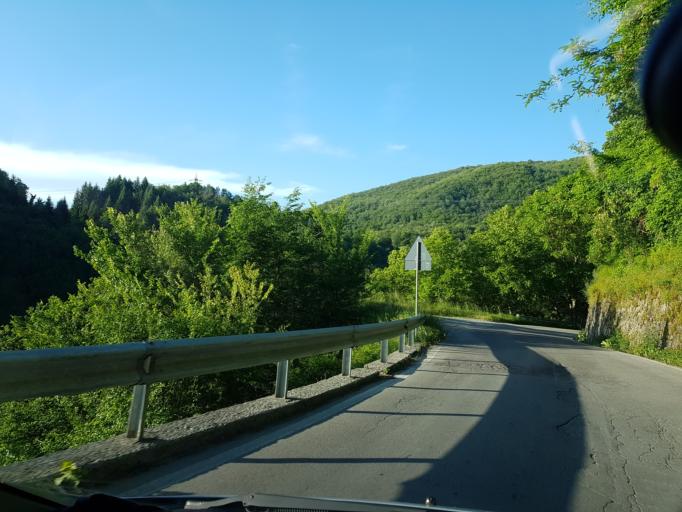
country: IT
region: Tuscany
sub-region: Provincia di Lucca
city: Minucciano
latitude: 44.1709
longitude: 10.2069
